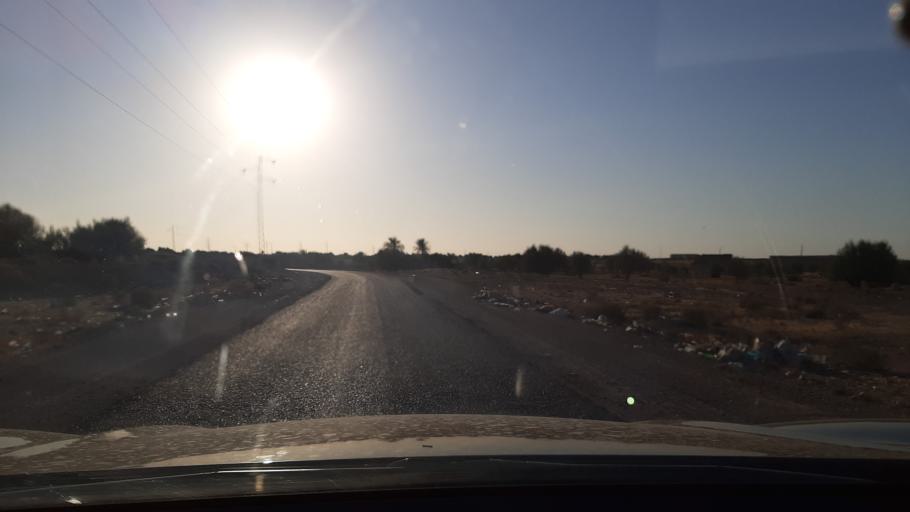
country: TN
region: Qabis
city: Matmata
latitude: 33.6164
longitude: 10.2448
